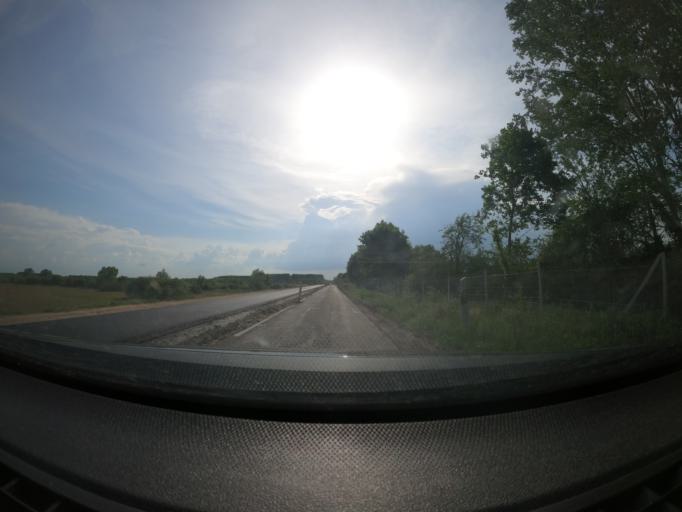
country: HU
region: Hajdu-Bihar
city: Vamospercs
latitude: 47.5263
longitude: 21.9608
